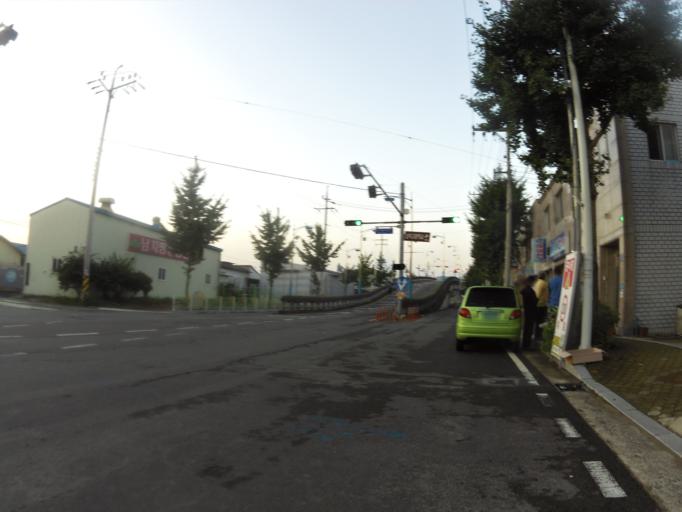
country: KR
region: Gyeongsangnam-do
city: Naeso
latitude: 35.3874
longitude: 128.4735
